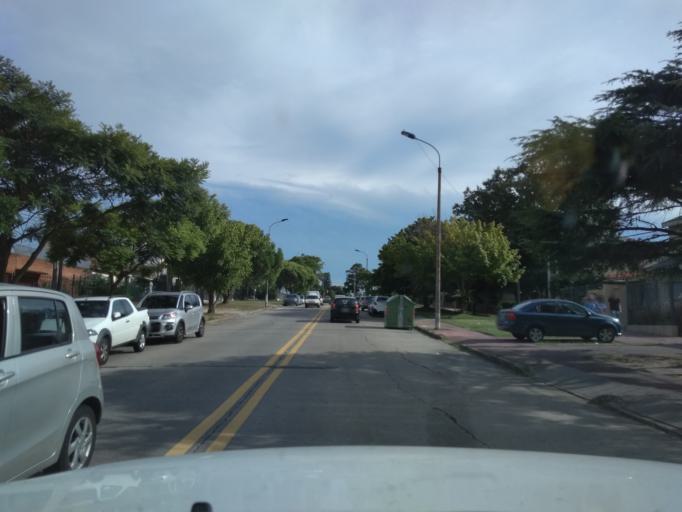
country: UY
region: Canelones
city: Paso de Carrasco
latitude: -34.8940
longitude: -56.0801
